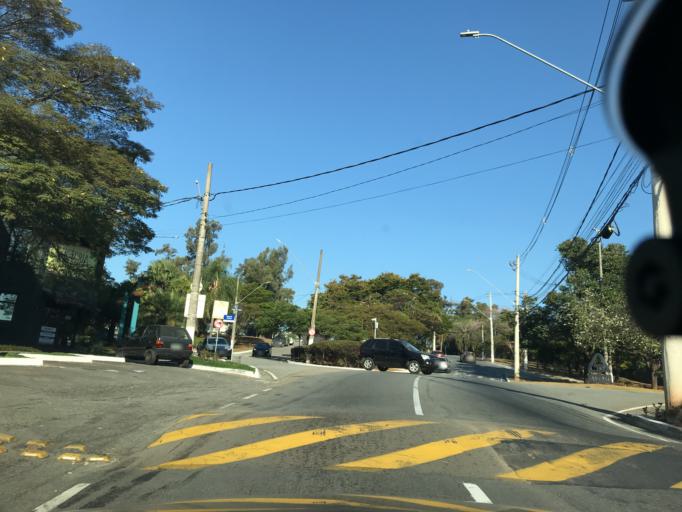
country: BR
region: Sao Paulo
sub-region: Santana De Parnaiba
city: Santana de Parnaiba
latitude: -23.4639
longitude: -46.8780
